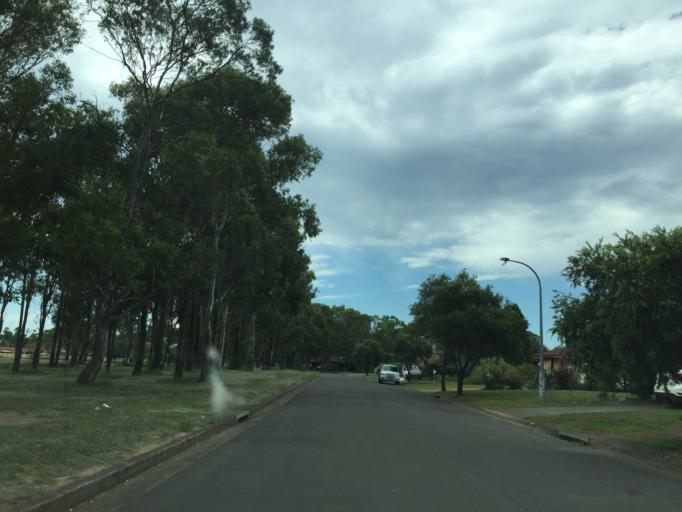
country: AU
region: New South Wales
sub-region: Blacktown
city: Mount Druitt
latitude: -33.8041
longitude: 150.7869
